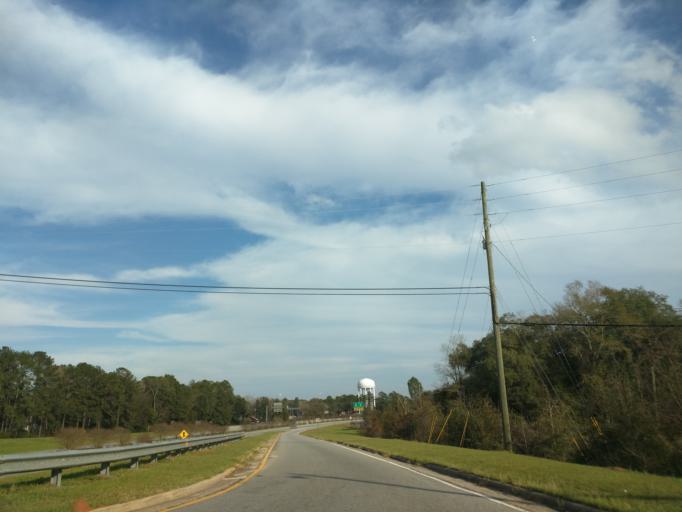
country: US
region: Georgia
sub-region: Decatur County
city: Bainbridge
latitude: 30.8917
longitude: -84.5763
